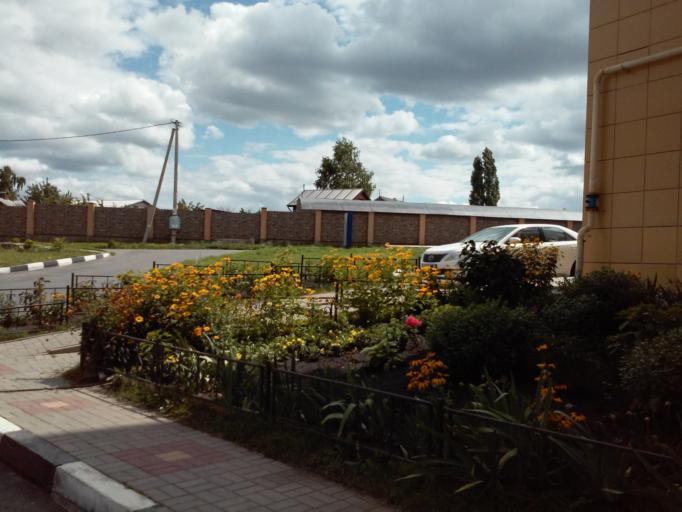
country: RU
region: Belgorod
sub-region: Belgorodskiy Rayon
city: Belgorod
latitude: 50.5346
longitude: 36.5757
